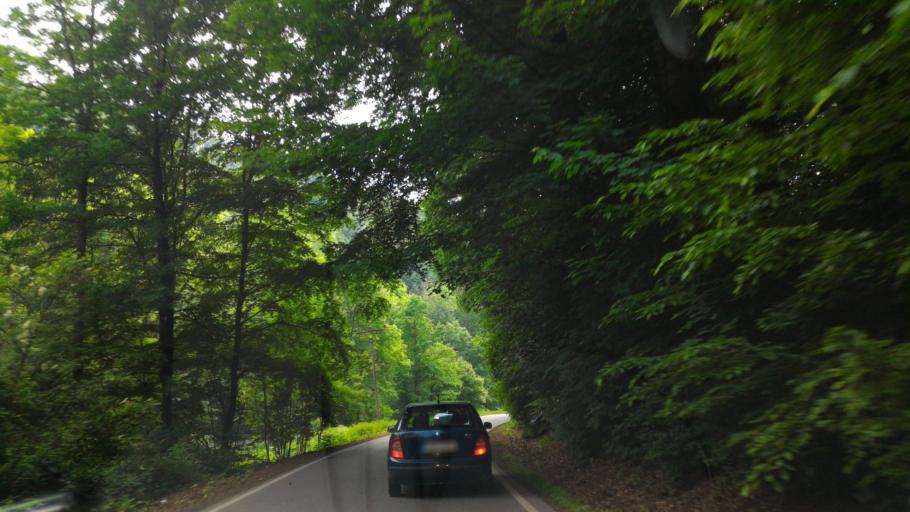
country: CZ
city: Chrastava
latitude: 50.7816
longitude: 14.9568
